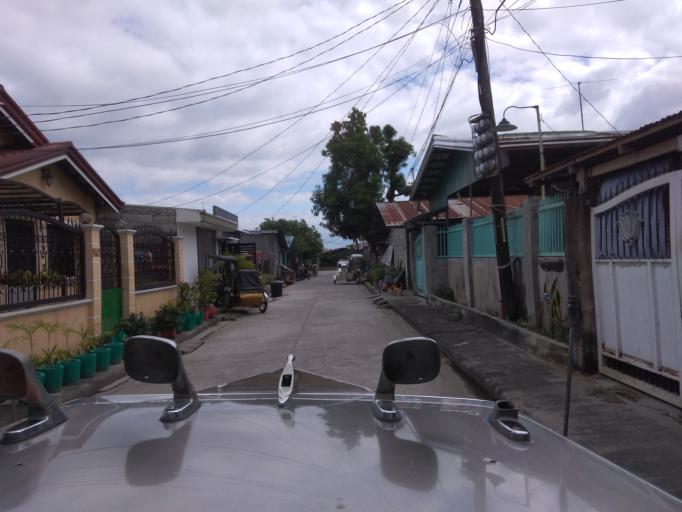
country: PH
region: Central Luzon
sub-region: Province of Pampanga
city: Pandacaqui
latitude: 15.1746
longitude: 120.6502
